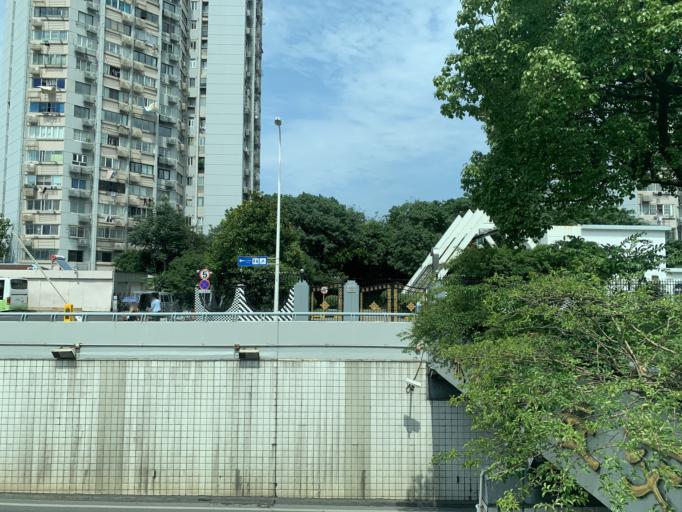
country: CN
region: Shanghai Shi
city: Pudong
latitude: 31.2327
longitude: 121.5202
